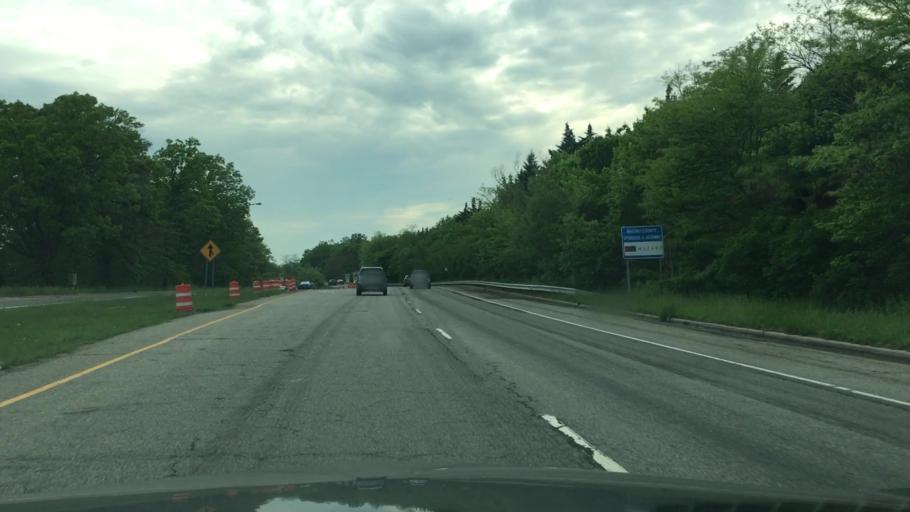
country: US
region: New York
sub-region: Nassau County
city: Jericho
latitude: 40.7899
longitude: -73.5218
